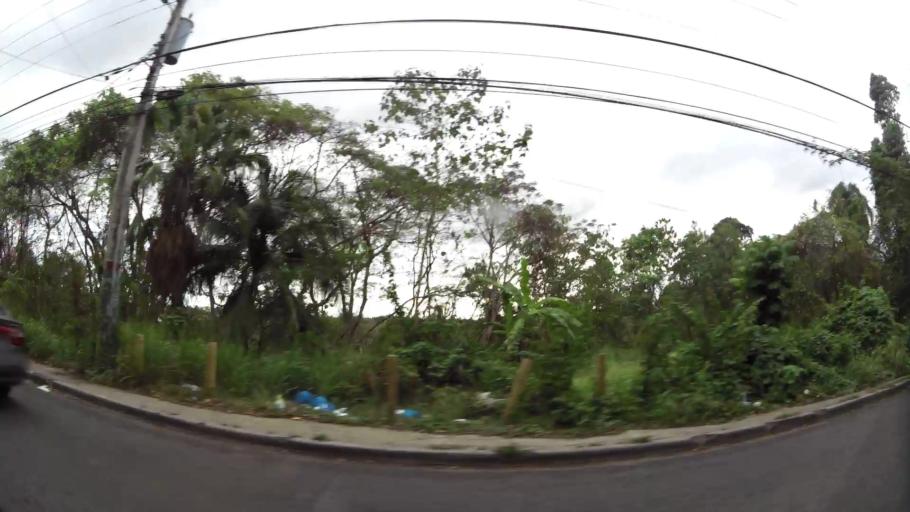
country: DO
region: Nacional
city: La Agustina
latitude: 18.5090
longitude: -69.9518
